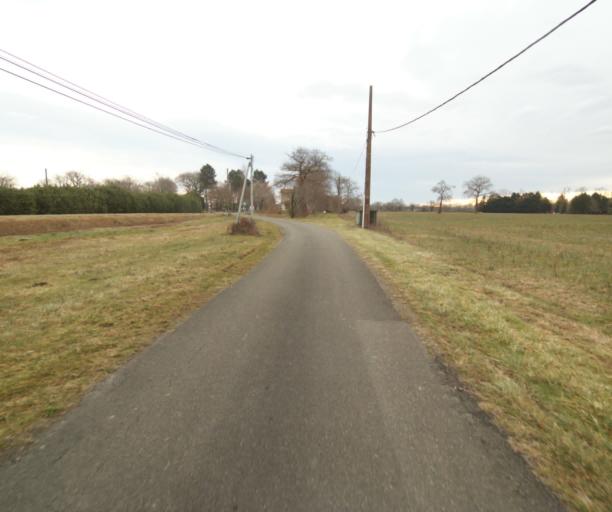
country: FR
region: Aquitaine
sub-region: Departement des Landes
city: Gabarret
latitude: 44.0145
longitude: -0.0349
